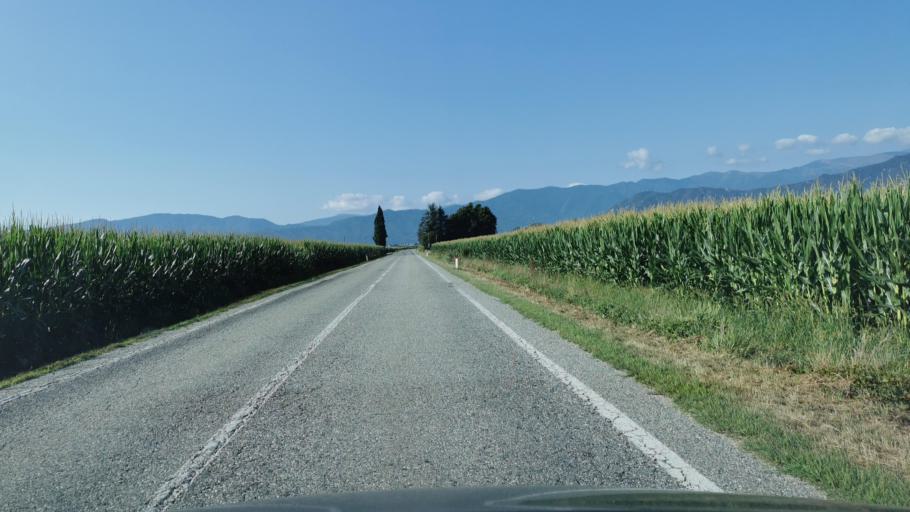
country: IT
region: Piedmont
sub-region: Provincia di Cuneo
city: Carde
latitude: 44.7052
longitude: 7.4356
